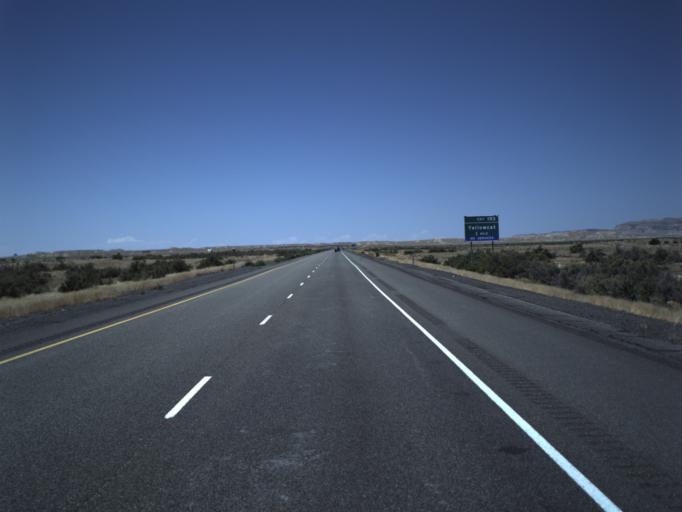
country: US
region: Utah
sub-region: Grand County
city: Moab
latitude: 38.9428
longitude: -109.5902
